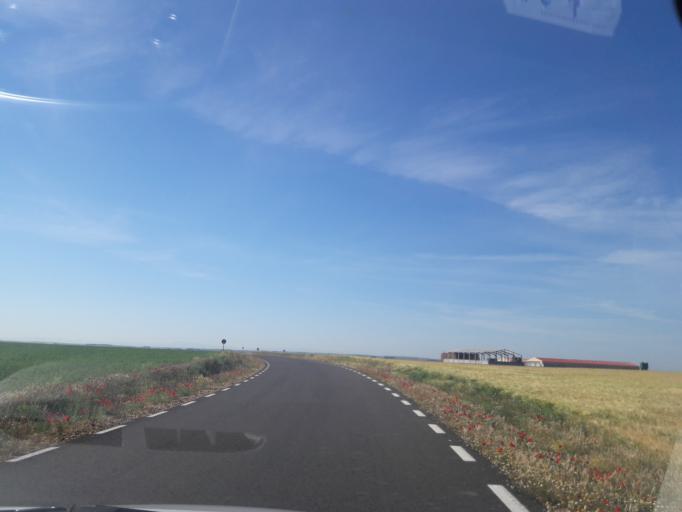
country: ES
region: Castille and Leon
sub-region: Provincia de Salamanca
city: Parada de Rubiales
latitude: 41.1303
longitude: -5.4302
